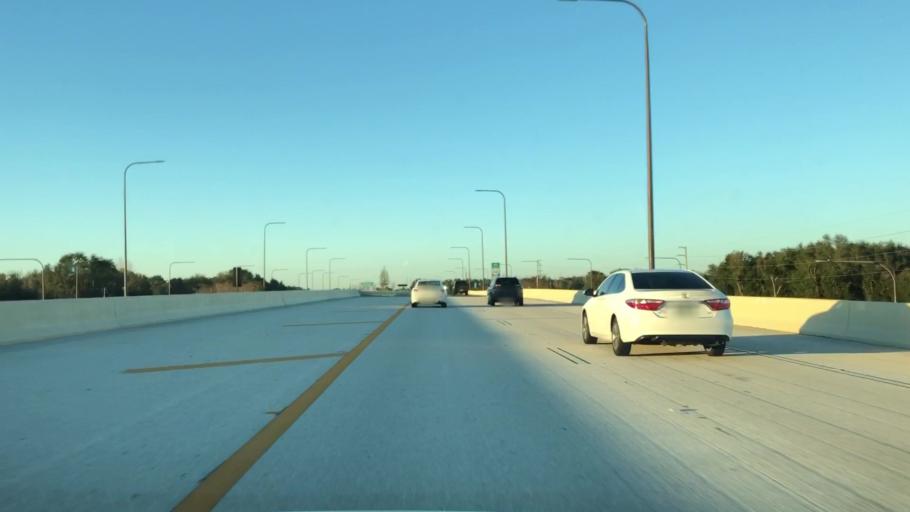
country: US
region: Florida
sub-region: Orange County
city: Apopka
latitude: 28.6983
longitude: -81.5591
